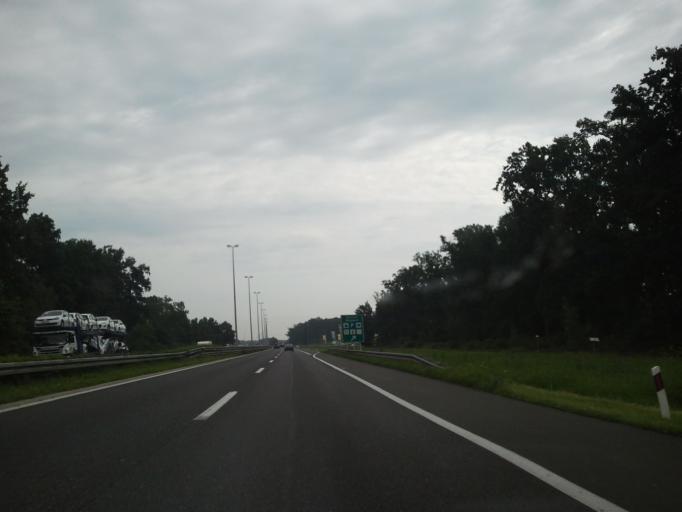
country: HR
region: Karlovacka
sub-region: Grad Karlovac
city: Karlovac
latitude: 45.5540
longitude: 15.6030
